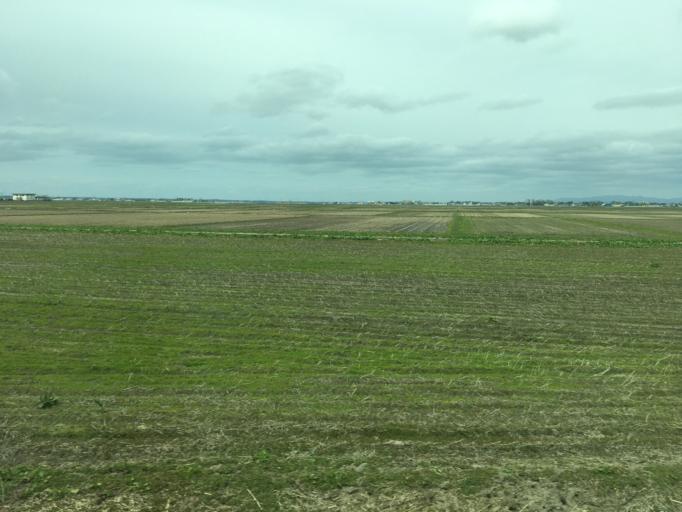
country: JP
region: Aomori
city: Goshogawara
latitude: 40.8101
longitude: 140.4201
